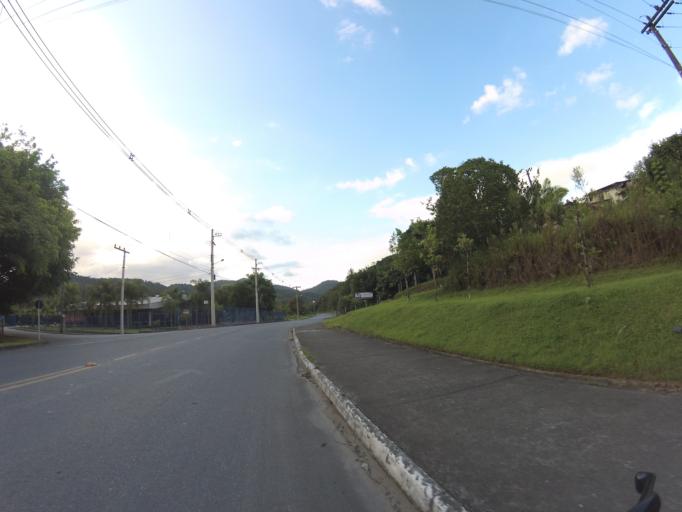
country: BR
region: Santa Catarina
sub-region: Pomerode
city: Pomerode
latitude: -26.8189
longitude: -49.1600
